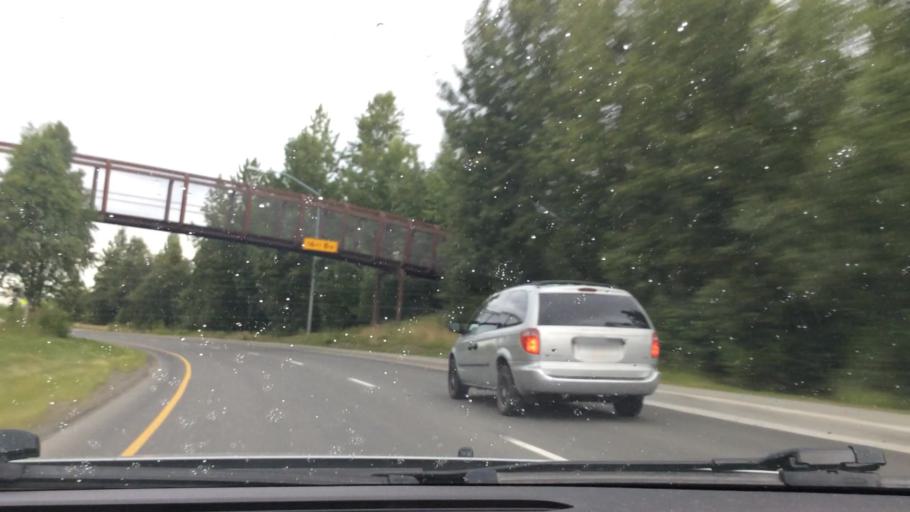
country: US
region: Alaska
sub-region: Anchorage Municipality
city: Anchorage
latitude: 61.1984
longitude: -149.7983
